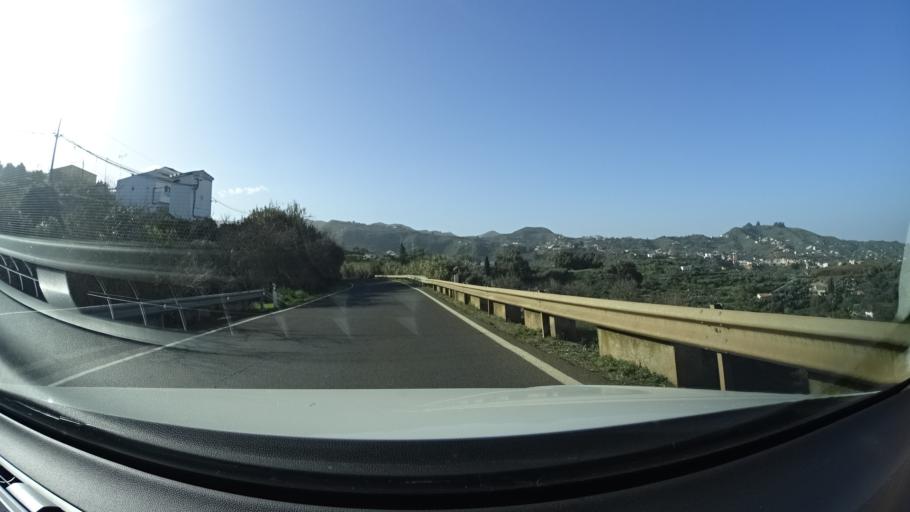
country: ES
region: Canary Islands
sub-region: Provincia de Las Palmas
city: Vega de San Mateo
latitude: 28.0156
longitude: -15.5376
